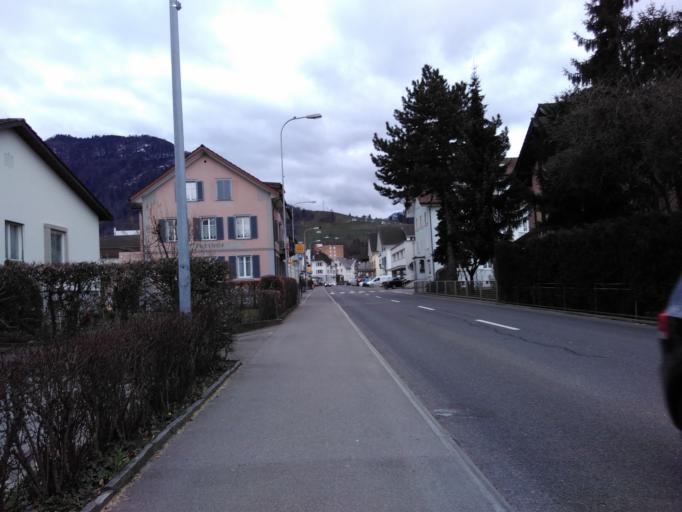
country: CH
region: Schwyz
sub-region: Bezirk March
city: Schubelbach
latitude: 47.1797
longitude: 8.8979
